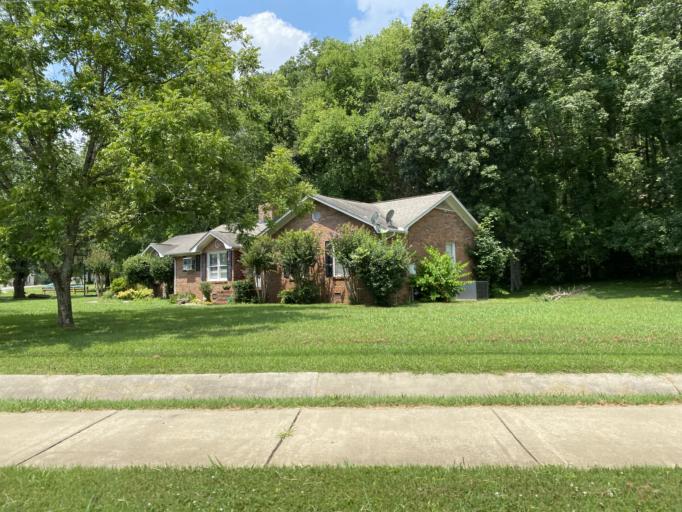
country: US
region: Alabama
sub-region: Madison County
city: Owens Cross Roads
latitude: 34.6511
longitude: -86.4842
